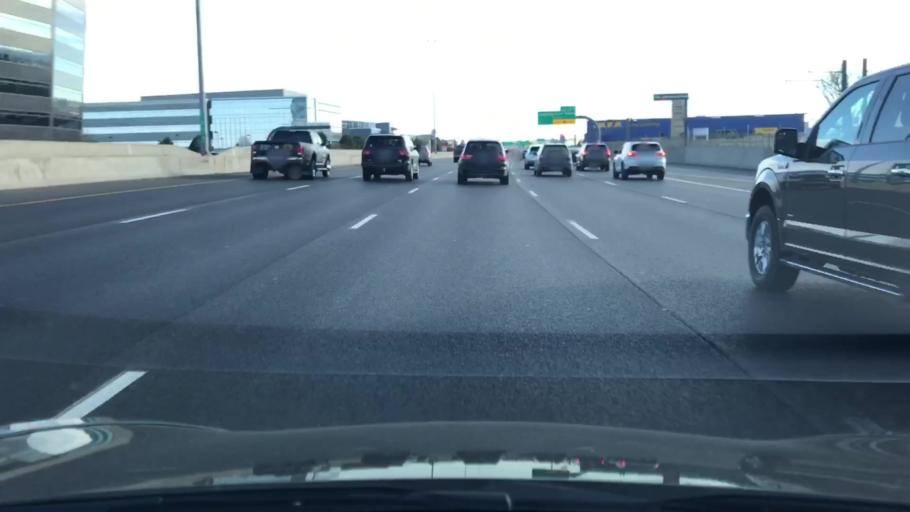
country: US
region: Colorado
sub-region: Arapahoe County
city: Centennial
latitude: 39.5804
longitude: -104.8744
